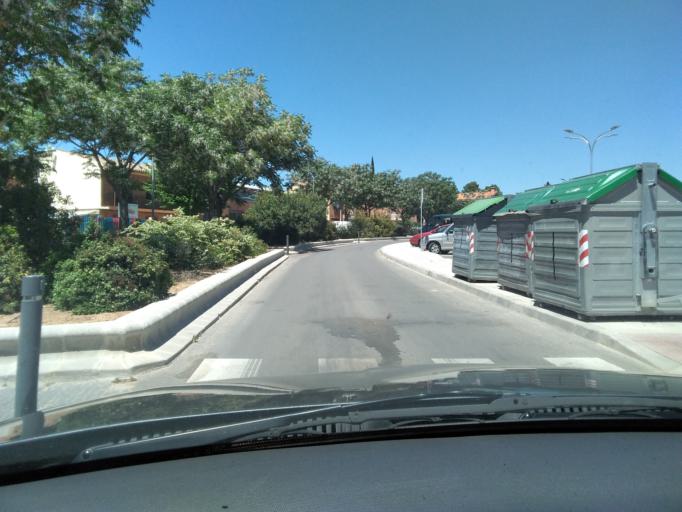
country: ES
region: Castille-La Mancha
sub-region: Province of Toledo
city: Toledo
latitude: 39.8667
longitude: -4.0415
